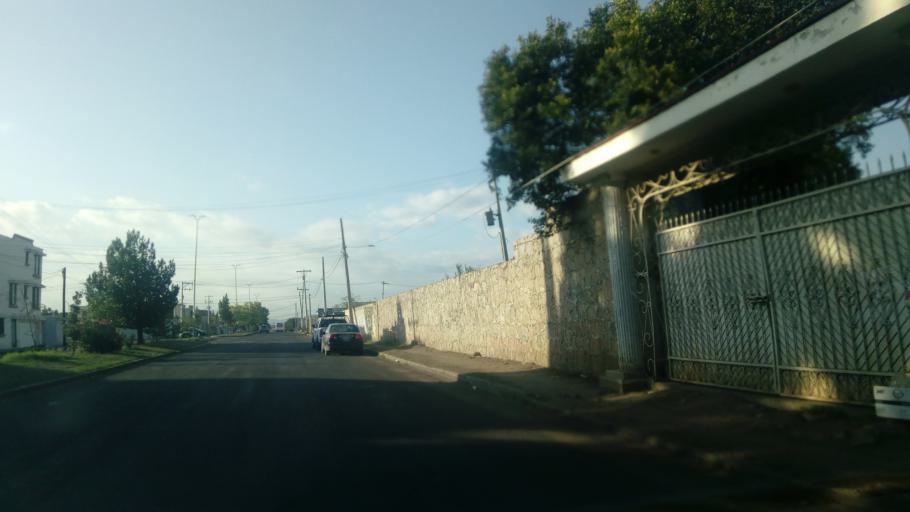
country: MX
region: Durango
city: Victoria de Durango
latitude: 24.0424
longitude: -104.6114
